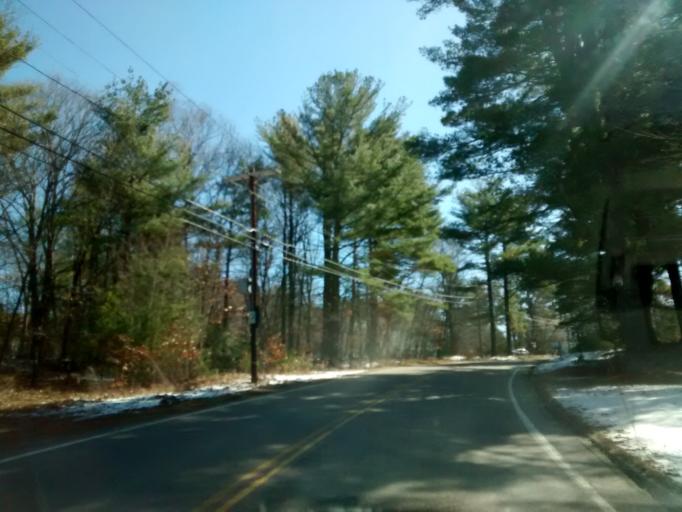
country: US
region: Massachusetts
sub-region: Worcester County
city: Whitinsville
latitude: 42.1199
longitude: -71.6871
